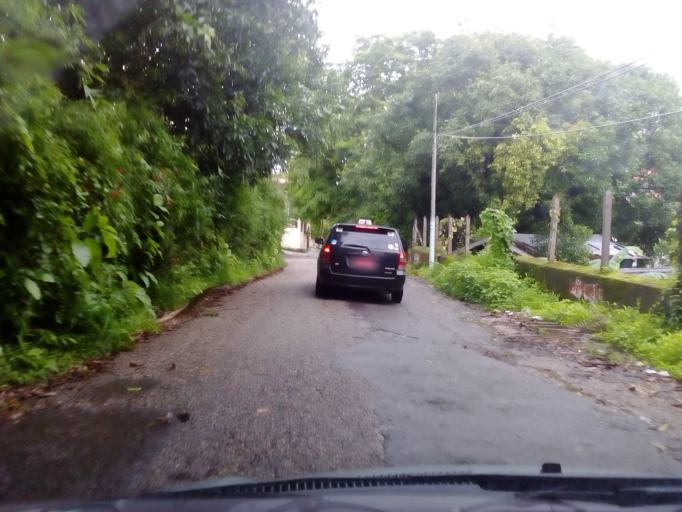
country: MM
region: Yangon
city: Yangon
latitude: 16.8213
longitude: 96.1509
